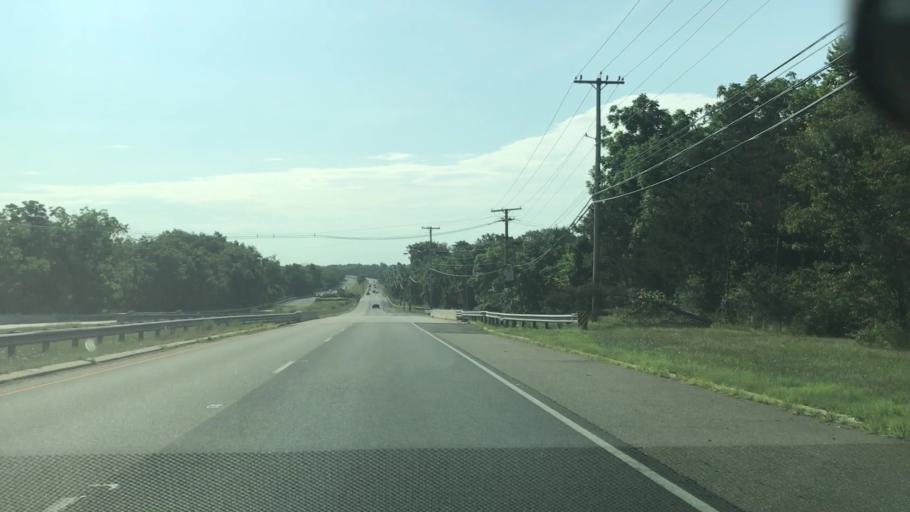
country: US
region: New Jersey
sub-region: Somerset County
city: Bridgewater
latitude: 40.5981
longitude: -74.6799
